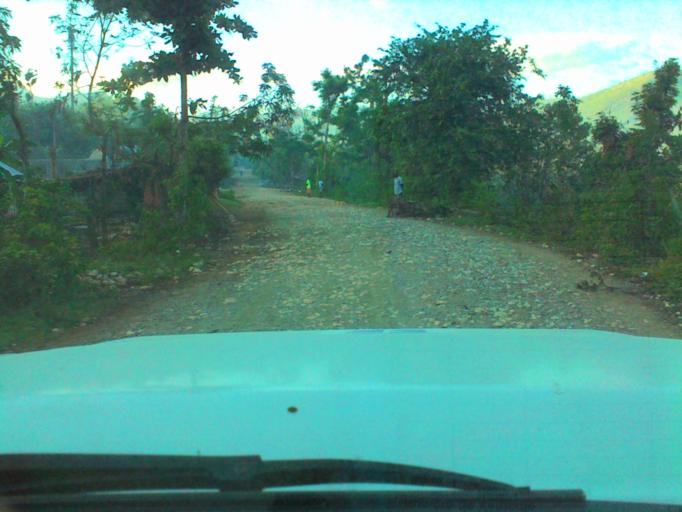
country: HT
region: Grandans
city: Jeremie
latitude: 18.5487
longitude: -74.1089
